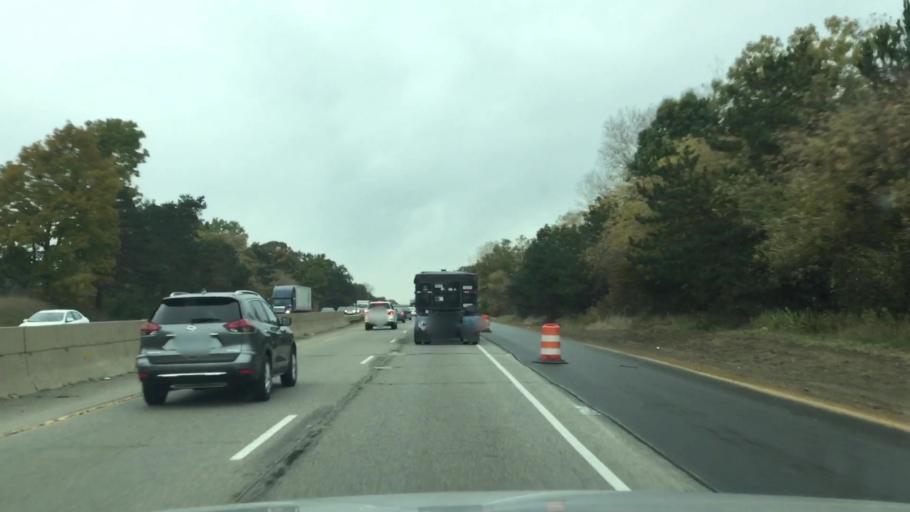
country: US
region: Michigan
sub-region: Jackson County
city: Michigan Center
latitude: 42.2775
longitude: -84.3269
